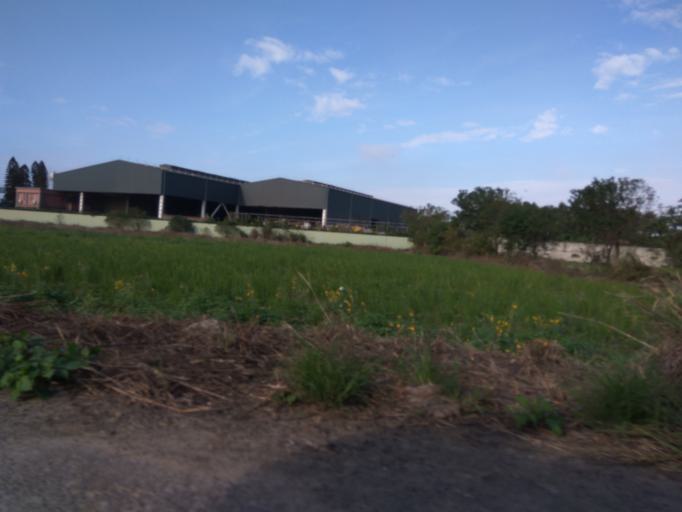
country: TW
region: Taiwan
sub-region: Hsinchu
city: Zhubei
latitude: 24.9840
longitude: 121.0381
